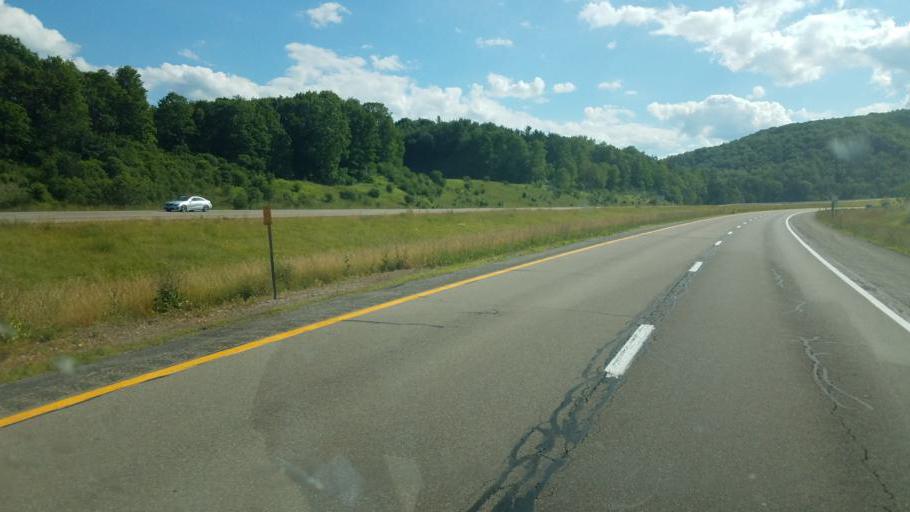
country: US
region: New York
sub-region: Allegany County
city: Alfred
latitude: 42.3183
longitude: -77.7481
